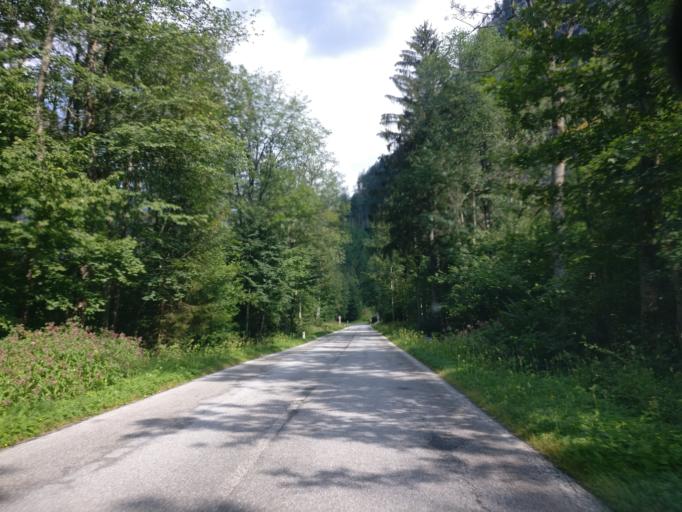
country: AT
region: Styria
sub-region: Politischer Bezirk Liezen
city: Johnsbach
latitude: 47.5809
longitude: 14.5437
